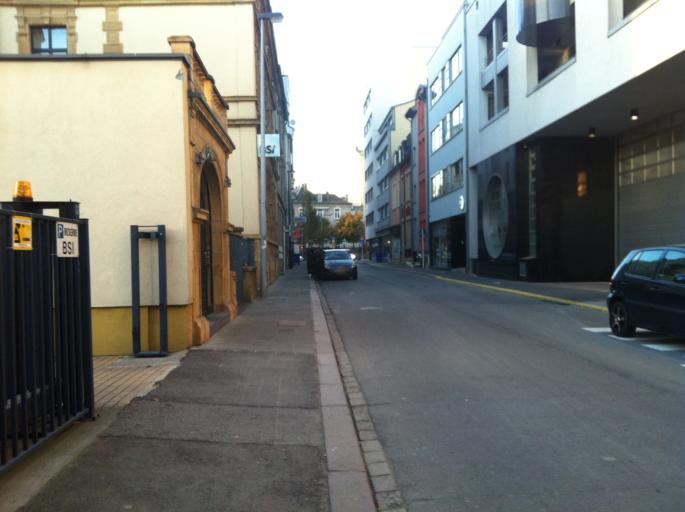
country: LU
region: Luxembourg
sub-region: Canton de Luxembourg
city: Luxembourg
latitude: 49.5994
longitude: 6.1282
